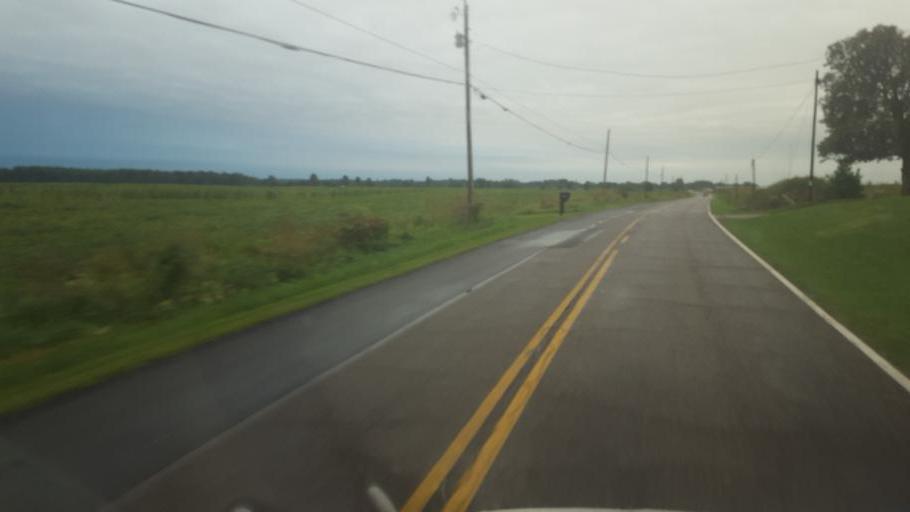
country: US
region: Ohio
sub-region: Licking County
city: Johnstown
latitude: 40.1958
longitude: -82.6919
